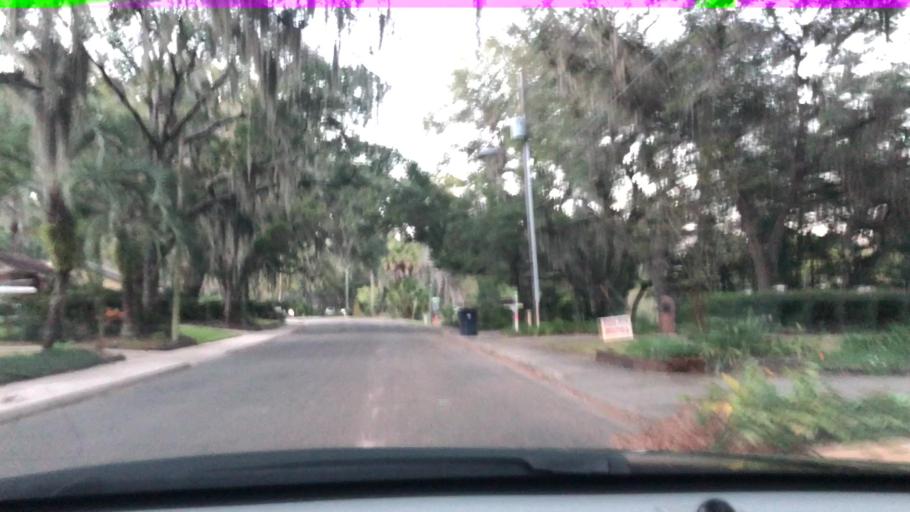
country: US
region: Florida
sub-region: Bay County
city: Panama City
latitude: 30.1433
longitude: -85.6444
